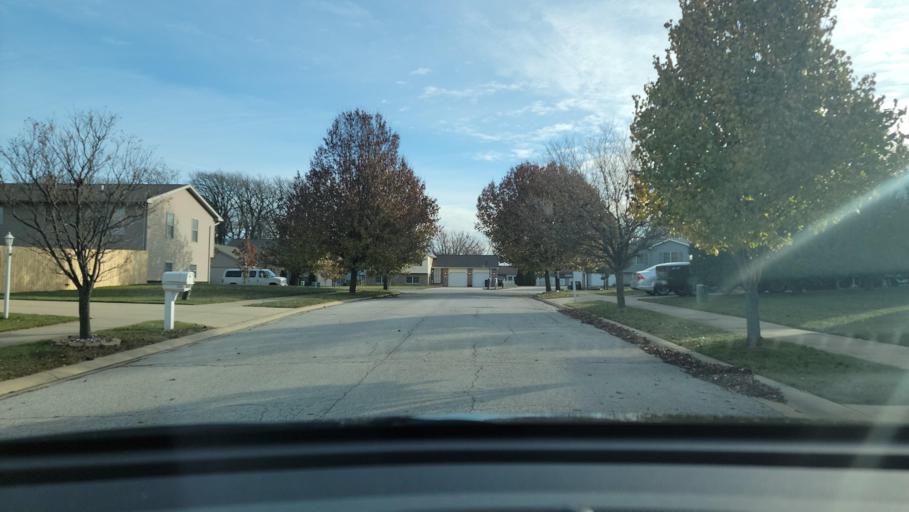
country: US
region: Indiana
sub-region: Porter County
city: Portage
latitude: 41.5618
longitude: -87.1744
